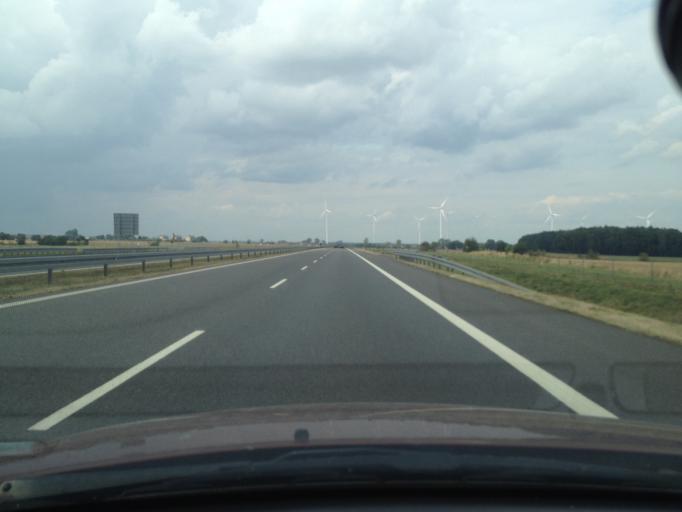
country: PL
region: West Pomeranian Voivodeship
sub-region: Powiat pyrzycki
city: Kozielice
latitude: 53.0917
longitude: 14.8299
